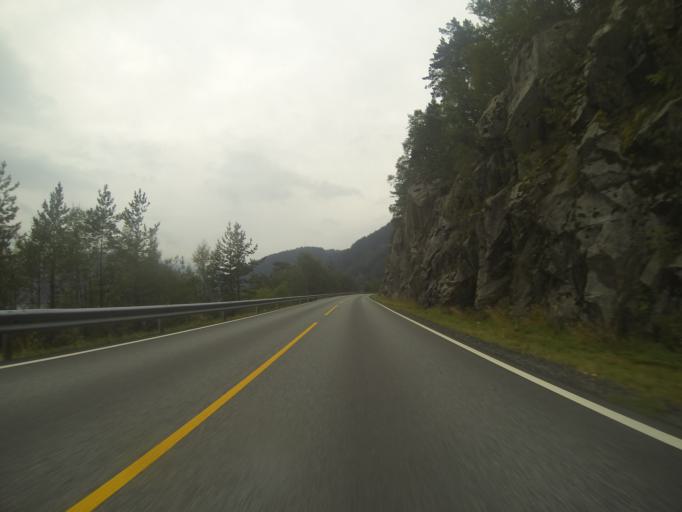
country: NO
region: Rogaland
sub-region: Suldal
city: Sand
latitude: 59.4722
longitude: 6.1873
